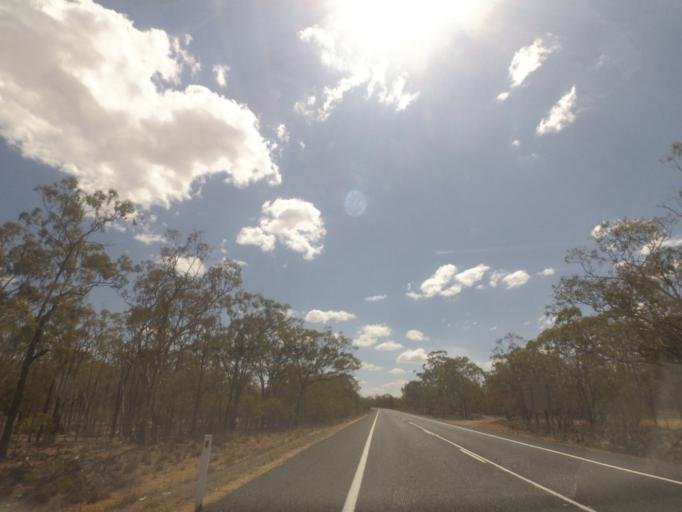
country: AU
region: Queensland
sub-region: Southern Downs
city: Warwick
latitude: -28.1629
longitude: 151.6794
